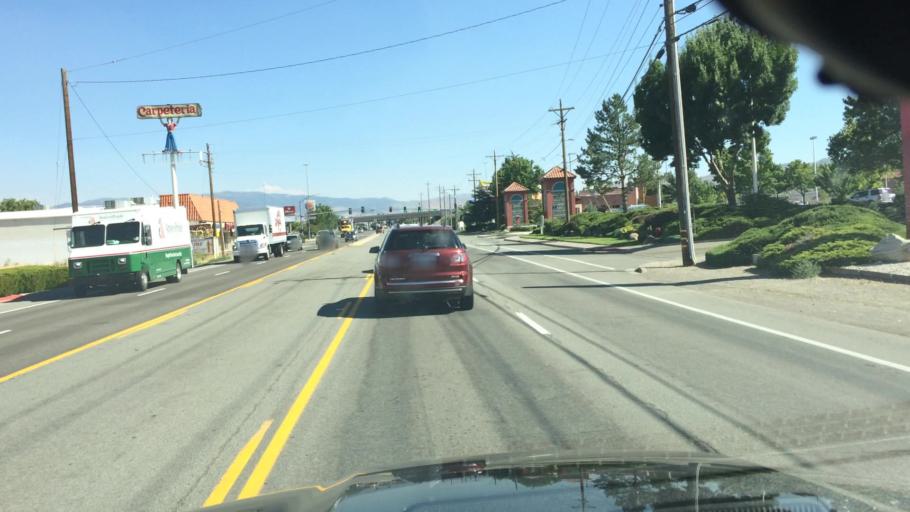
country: US
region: Nevada
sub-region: Washoe County
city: Reno
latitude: 39.4541
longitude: -119.7781
